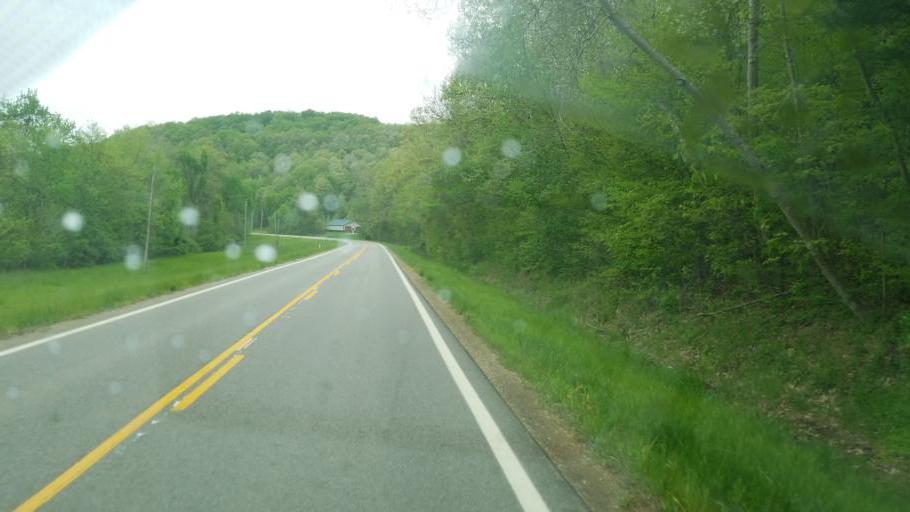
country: US
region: Ohio
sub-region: Guernsey County
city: Mantua
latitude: 40.1628
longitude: -81.6416
